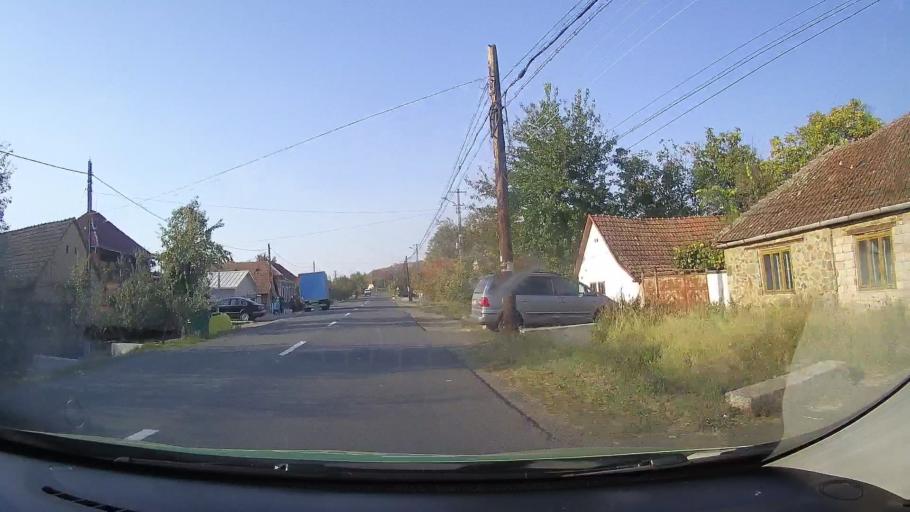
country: RO
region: Arad
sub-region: Comuna Ghioroc
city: Ghioroc
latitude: 46.1421
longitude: 21.6017
